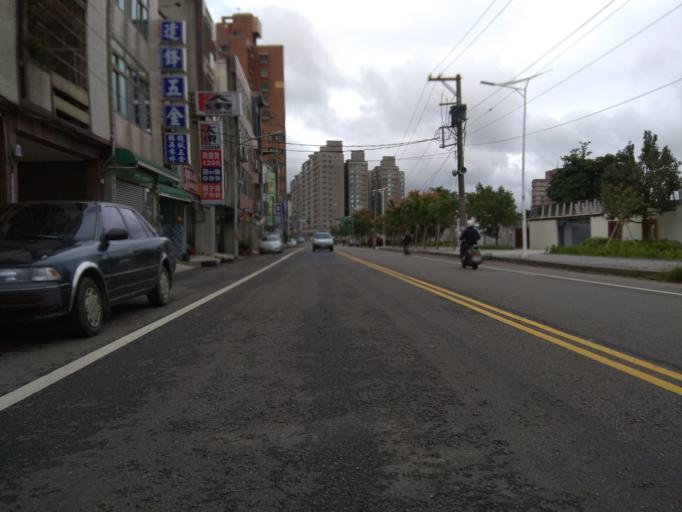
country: TW
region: Taiwan
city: Taoyuan City
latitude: 24.9596
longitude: 121.2180
